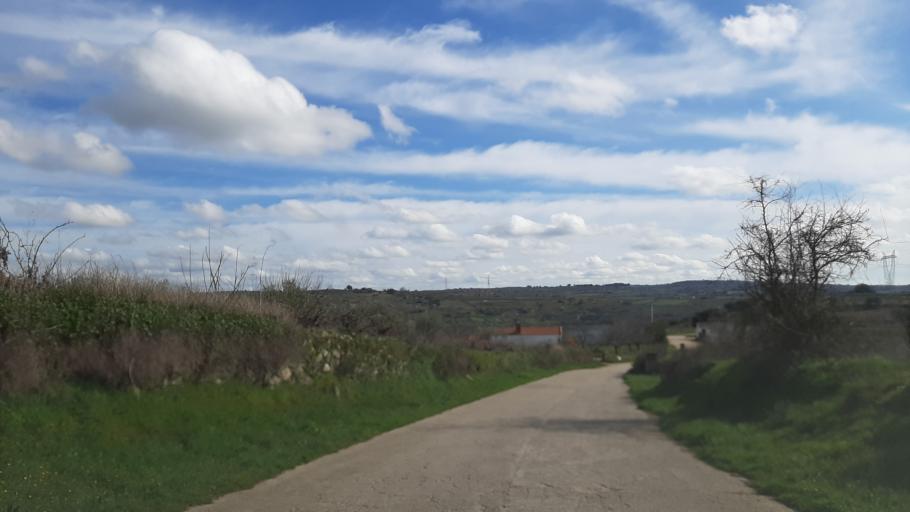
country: ES
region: Castille and Leon
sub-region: Provincia de Salamanca
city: Villarino de los Aires
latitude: 41.2496
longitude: -6.5234
